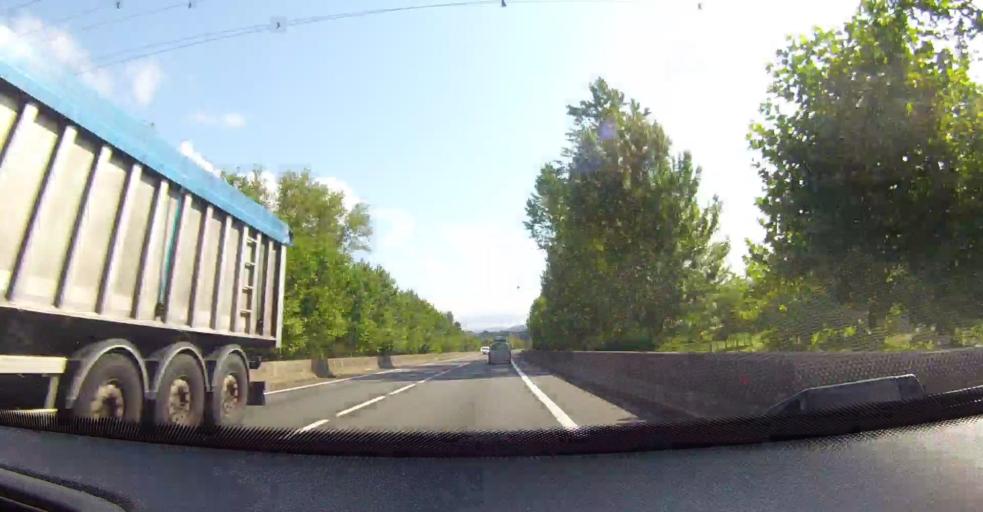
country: ES
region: Basque Country
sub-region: Bizkaia
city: Gernika-Lumo
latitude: 43.3117
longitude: -2.6725
